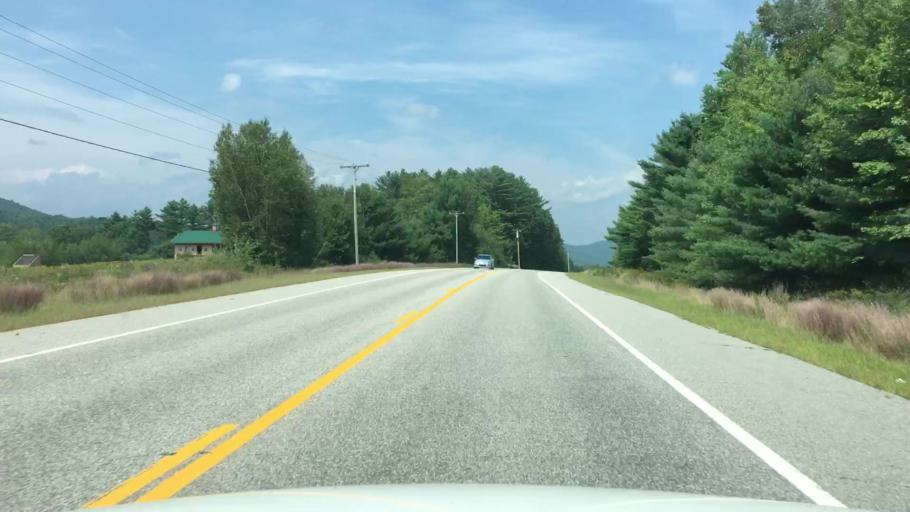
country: US
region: Maine
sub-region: Oxford County
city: Canton
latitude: 44.4574
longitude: -70.3195
